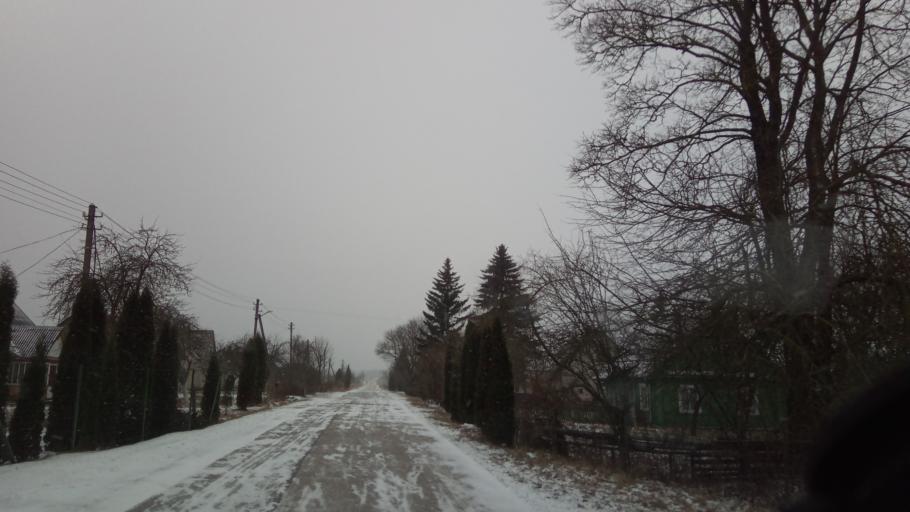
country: LT
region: Vilnius County
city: Ukmerge
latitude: 55.3061
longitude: 24.9738
